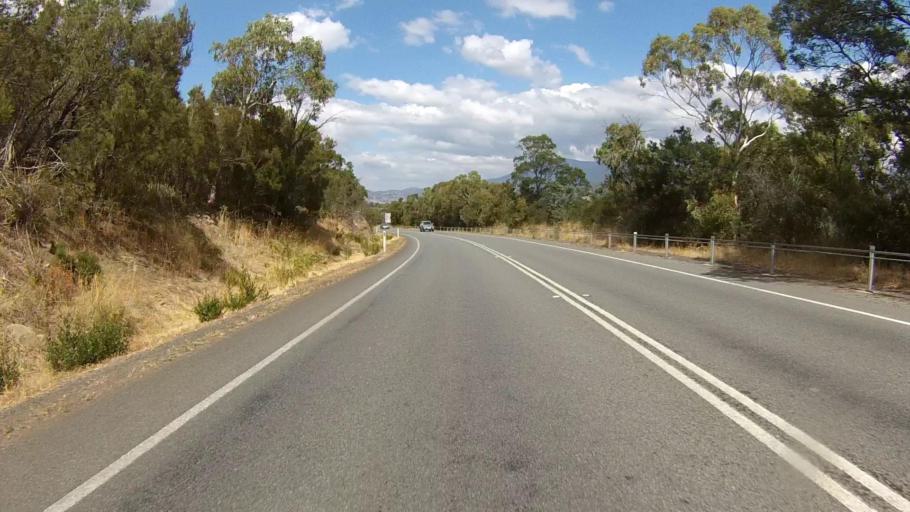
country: AU
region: Tasmania
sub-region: Brighton
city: Old Beach
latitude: -42.7725
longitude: 147.2686
